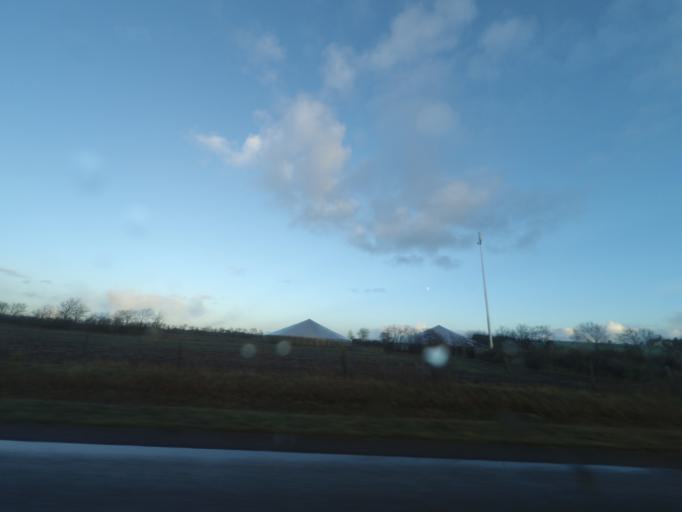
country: DK
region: Central Jutland
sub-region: Herning Kommune
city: Lind
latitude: 56.0251
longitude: 9.0099
